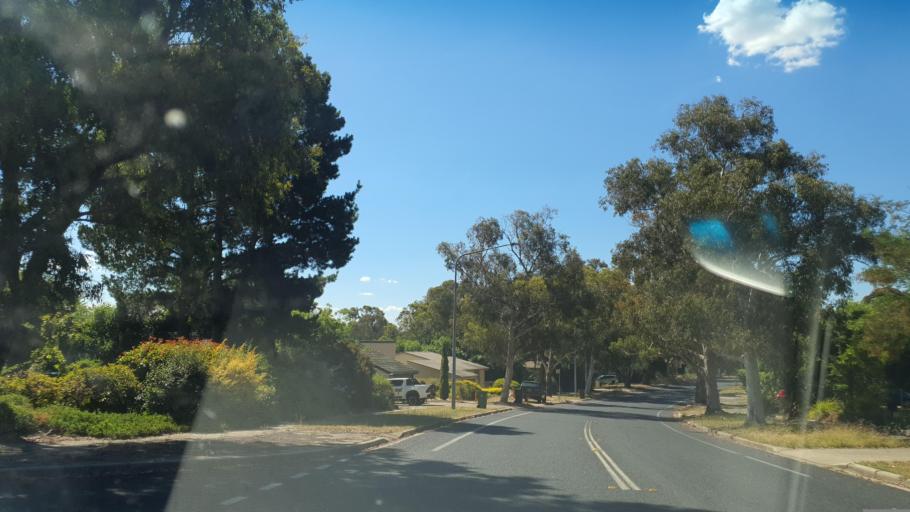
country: AU
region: Australian Capital Territory
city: Belconnen
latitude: -35.2118
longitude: 149.0433
